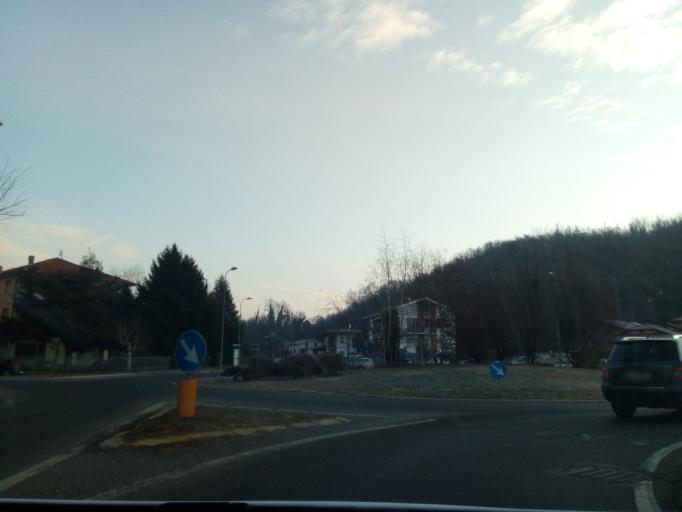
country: IT
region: Piedmont
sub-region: Provincia di Torino
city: Pavone Canavese
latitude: 45.4438
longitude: 7.8547
